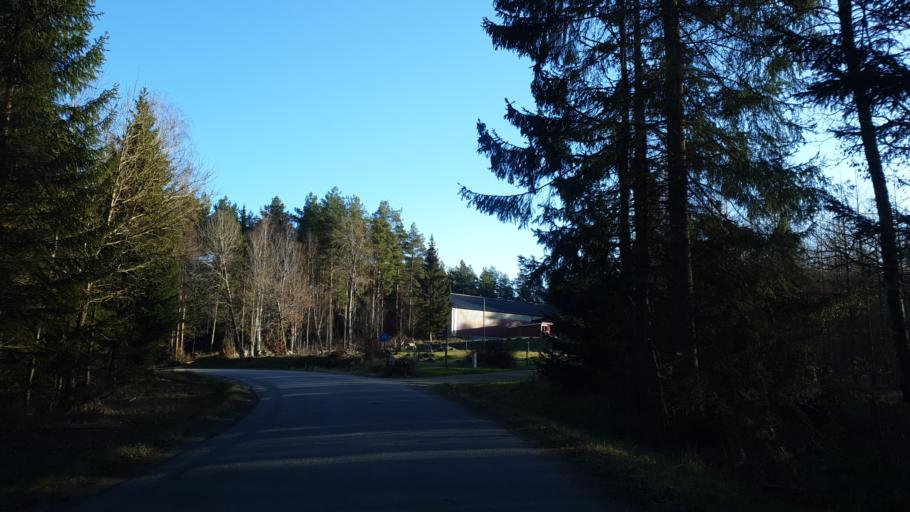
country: SE
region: Blekinge
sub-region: Ronneby Kommun
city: Brakne-Hoby
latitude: 56.2308
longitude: 15.1637
